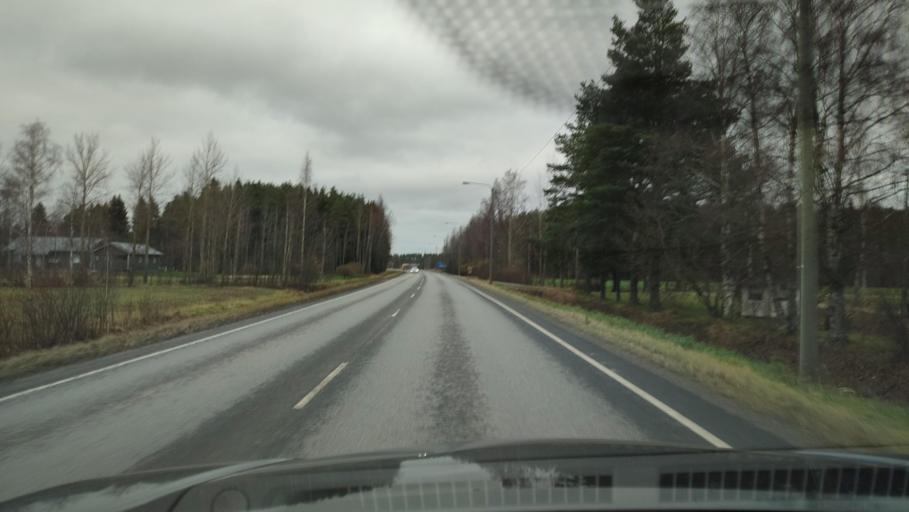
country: FI
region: Southern Ostrobothnia
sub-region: Seinaejoki
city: Kurikka
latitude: 62.6786
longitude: 22.4736
